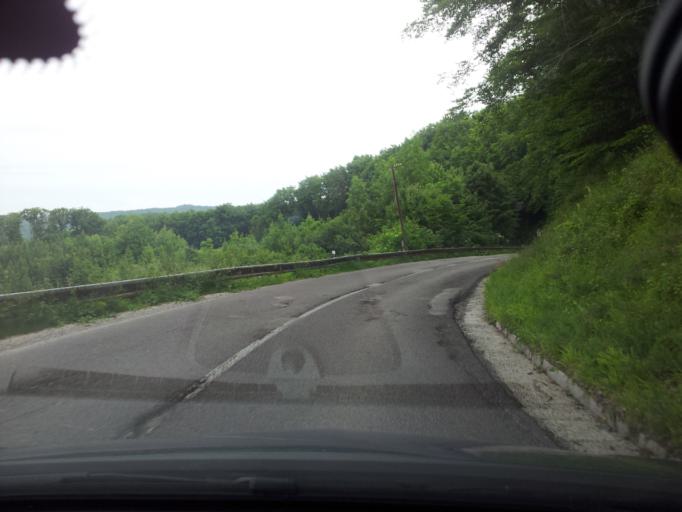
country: SK
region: Nitriansky
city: Partizanske
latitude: 48.5384
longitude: 18.4454
